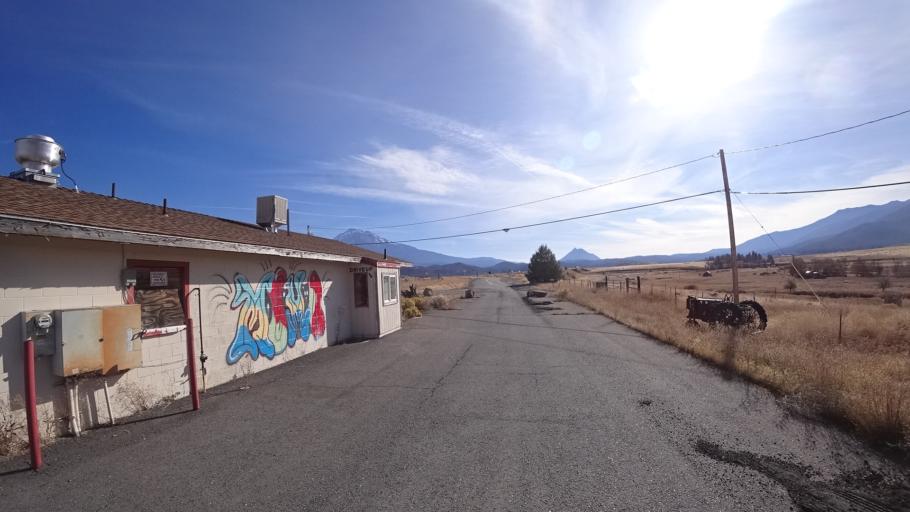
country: US
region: California
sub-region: Siskiyou County
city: Weed
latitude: 41.4761
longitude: -122.4565
